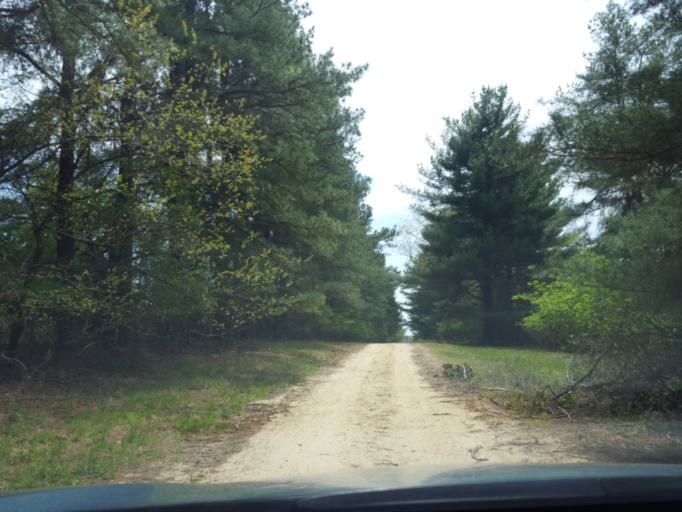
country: US
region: Maryland
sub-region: Calvert County
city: Dunkirk
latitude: 38.7356
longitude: -76.7023
